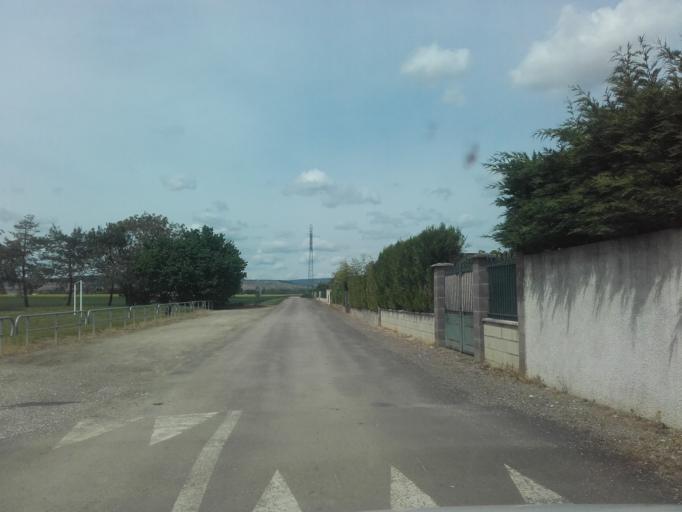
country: FR
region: Bourgogne
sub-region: Departement de la Cote-d'Or
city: Bligny-les-Beaune
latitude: 46.9927
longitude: 4.8440
